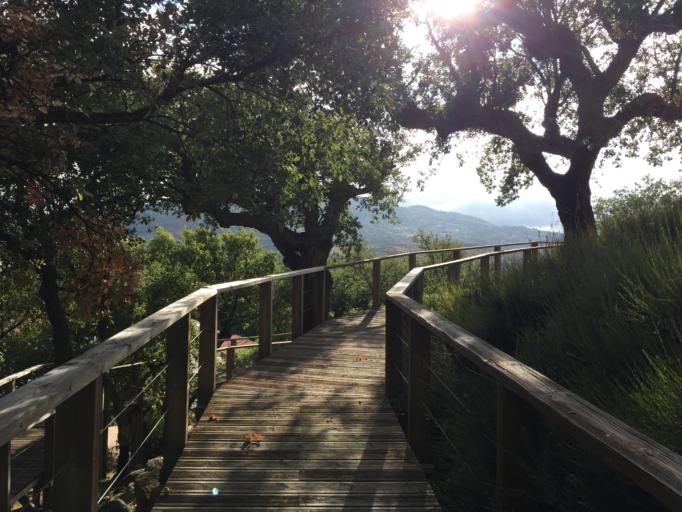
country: PT
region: Portalegre
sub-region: Marvao
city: Marvao
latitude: 39.4120
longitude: -7.3501
